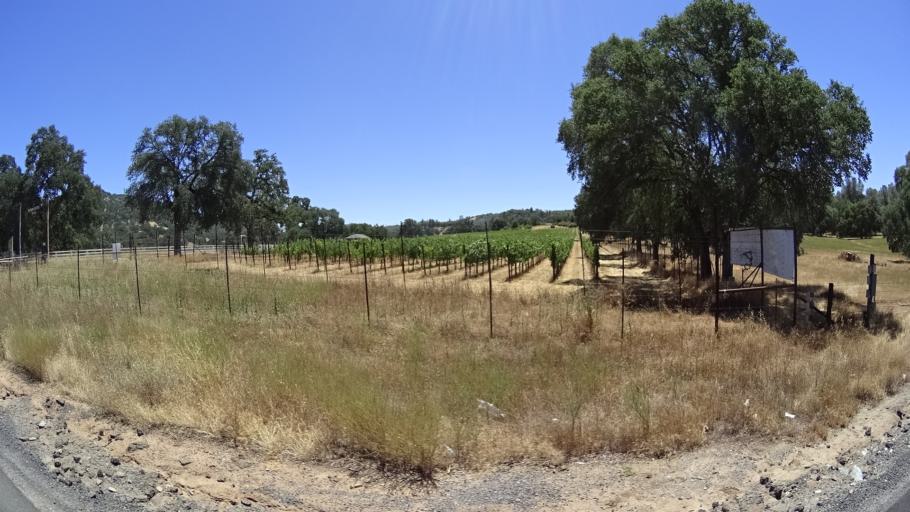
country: US
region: California
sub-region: Calaveras County
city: Copperopolis
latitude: 38.0493
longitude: -120.6316
